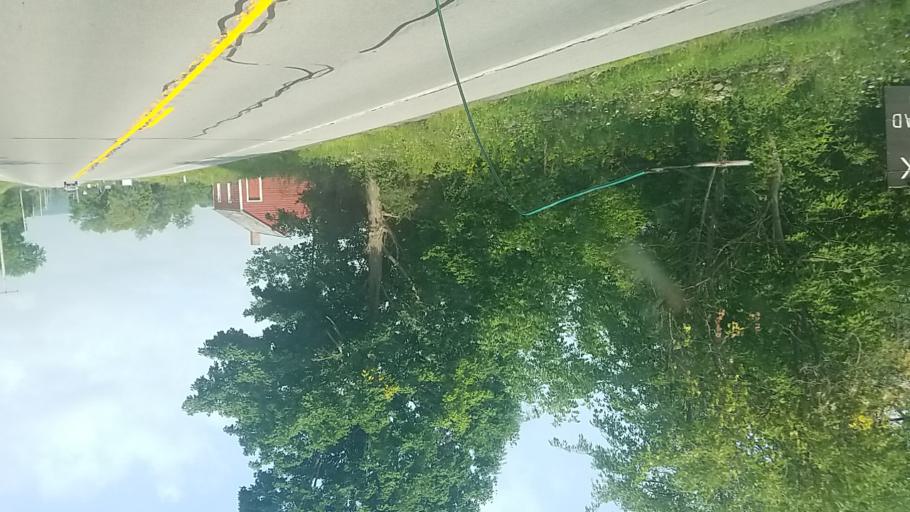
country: US
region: New York
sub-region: Montgomery County
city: Saint Johnsville
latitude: 42.9851
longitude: -74.6469
